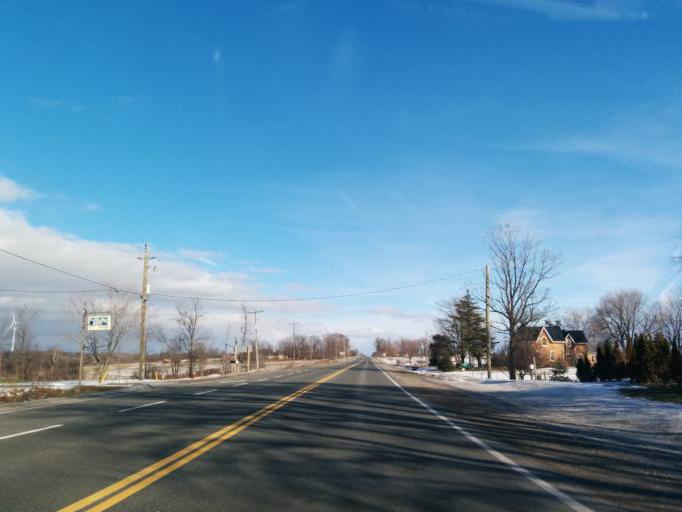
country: CA
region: Ontario
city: Ancaster
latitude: 42.9371
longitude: -79.9114
